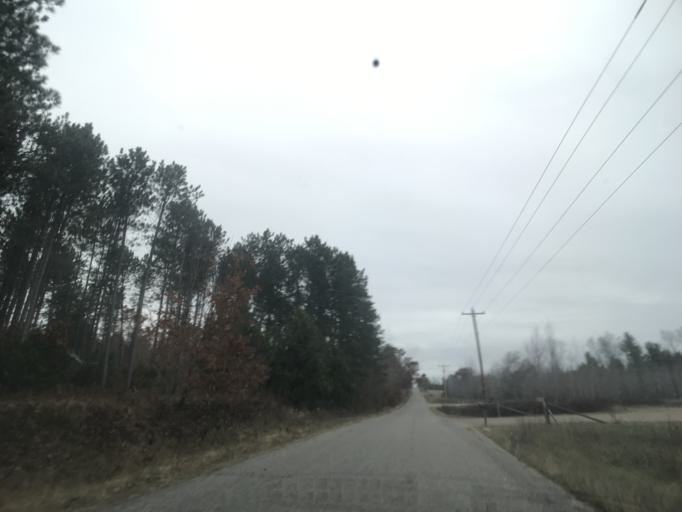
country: US
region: Wisconsin
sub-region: Menominee County
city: Legend Lake
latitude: 45.1679
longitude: -88.4560
